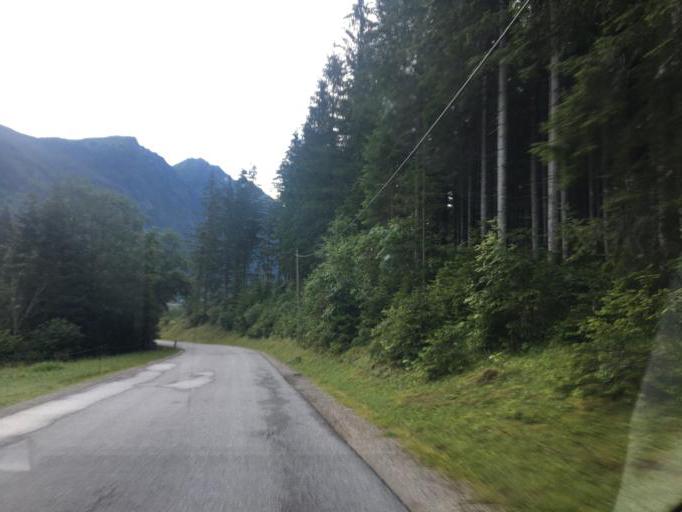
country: AT
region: Styria
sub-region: Politischer Bezirk Liezen
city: Schladming
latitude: 47.3571
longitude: 13.6952
